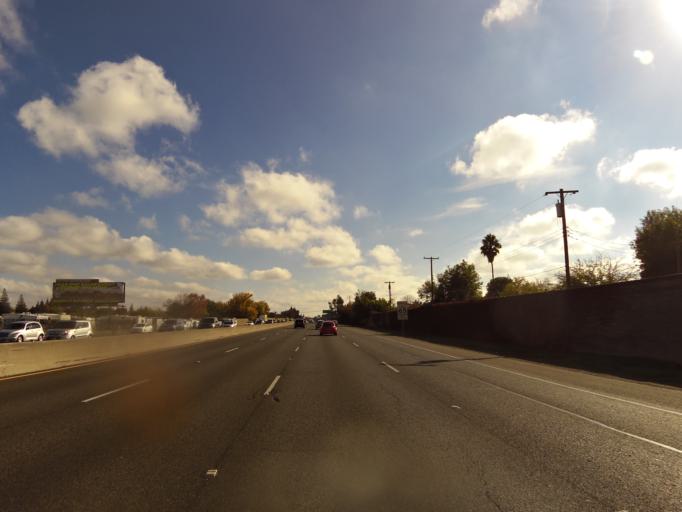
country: US
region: California
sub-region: Sacramento County
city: Parkway
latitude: 38.4906
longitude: -121.4403
